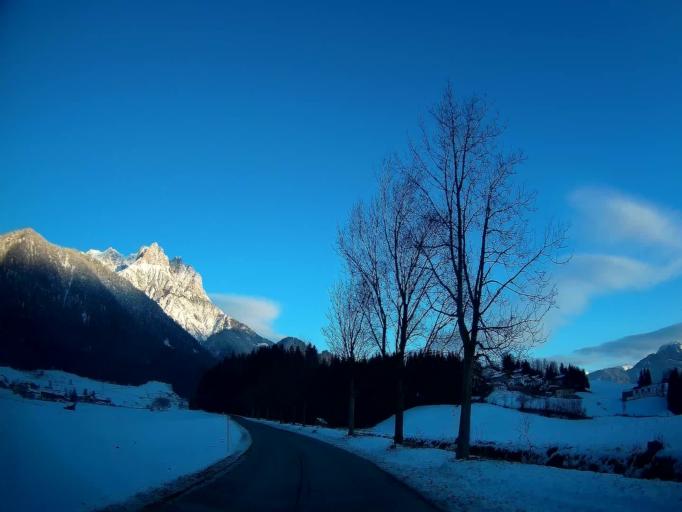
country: AT
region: Salzburg
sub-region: Politischer Bezirk Zell am See
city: Saalfelden am Steinernen Meer
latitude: 47.4516
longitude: 12.8246
